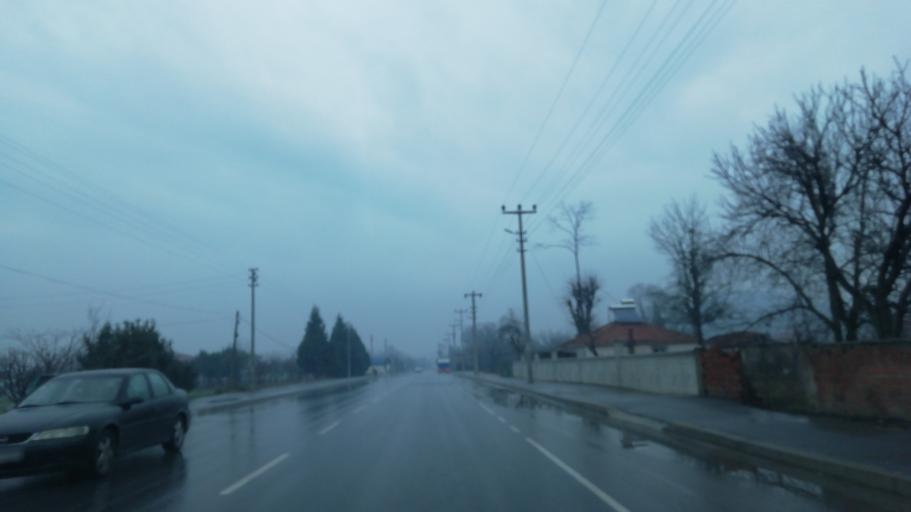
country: TR
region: Sakarya
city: Akyazi
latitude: 40.6454
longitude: 30.6212
